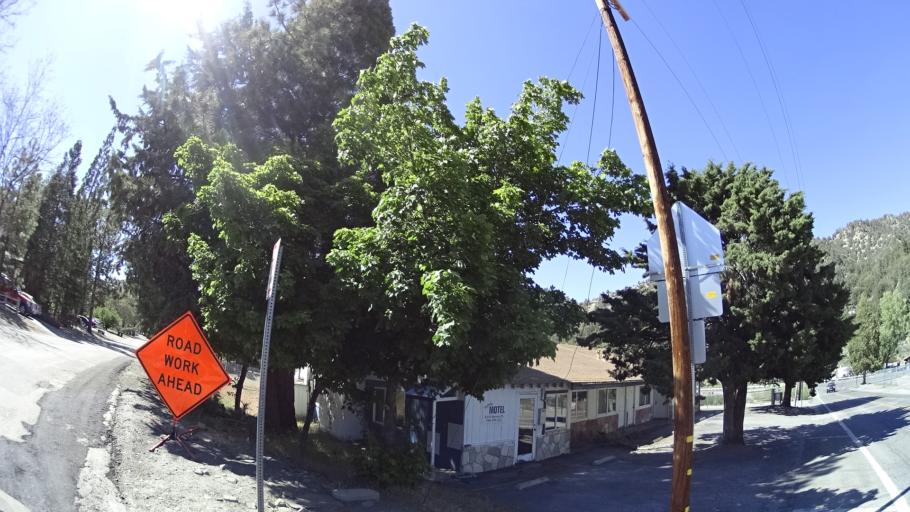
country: US
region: California
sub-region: San Bernardino County
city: Wrightwood
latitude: 34.3614
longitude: -117.6370
